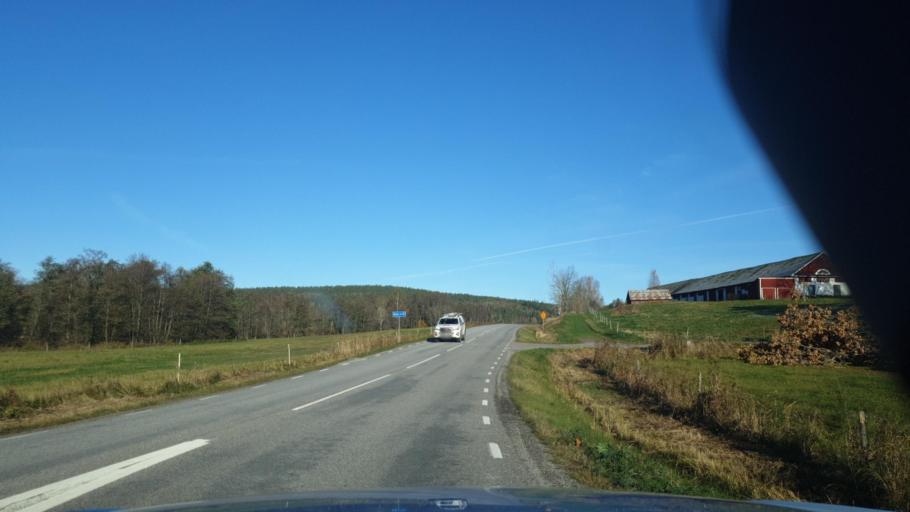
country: SE
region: Vaermland
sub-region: Grums Kommun
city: Grums
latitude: 59.3953
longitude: 13.0708
